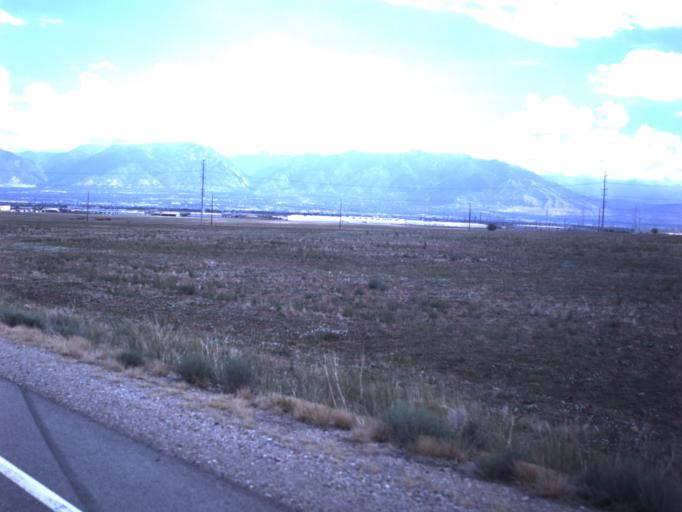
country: US
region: Utah
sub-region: Salt Lake County
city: Herriman
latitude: 40.5720
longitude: -112.0700
